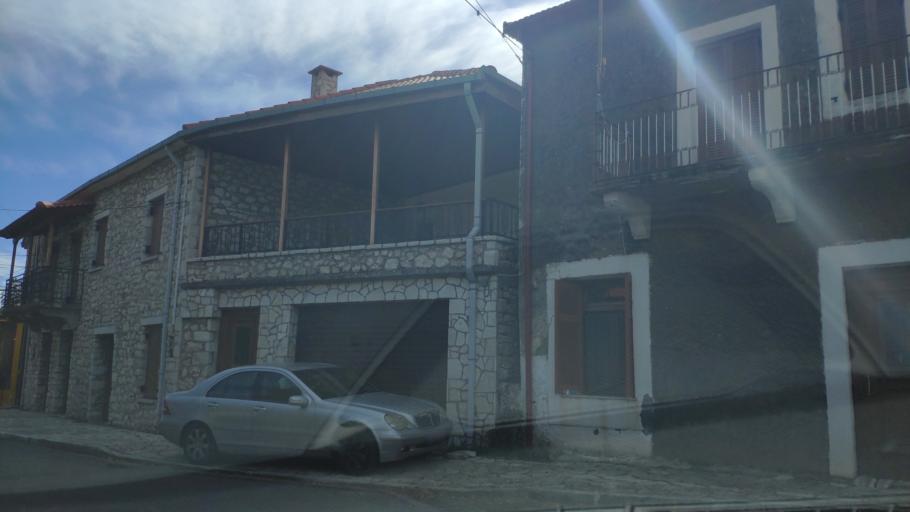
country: GR
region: Peloponnese
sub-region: Nomos Arkadias
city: Dimitsana
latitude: 37.5208
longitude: 22.0725
